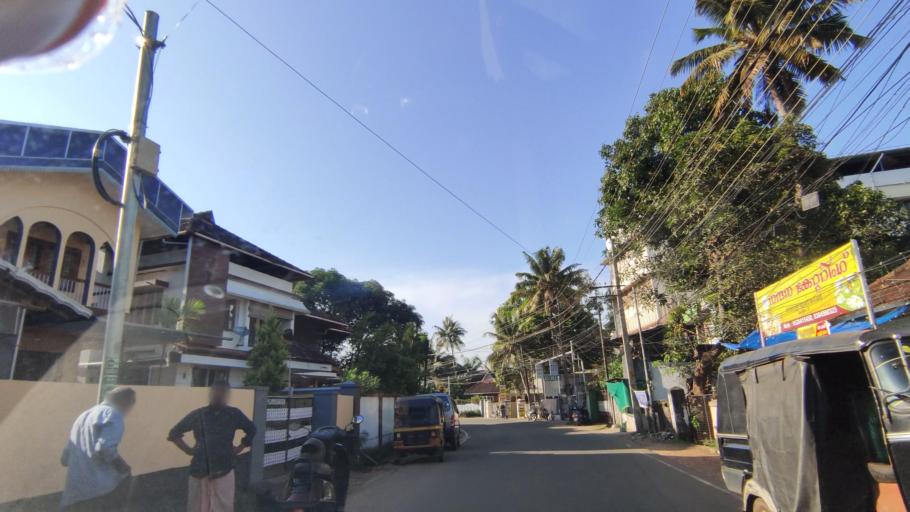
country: IN
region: Kerala
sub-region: Kottayam
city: Kottayam
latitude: 9.5907
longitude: 76.5151
